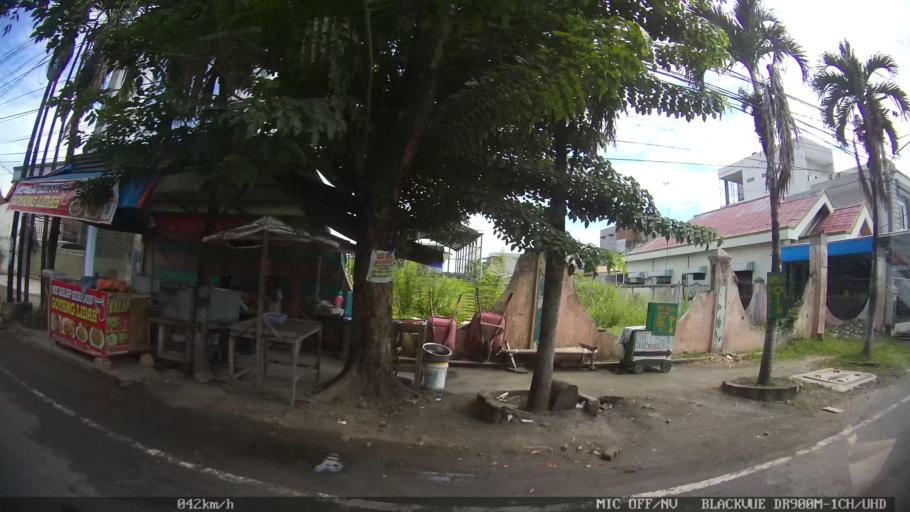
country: ID
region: North Sumatra
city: Medan
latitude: 3.6225
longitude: 98.6901
